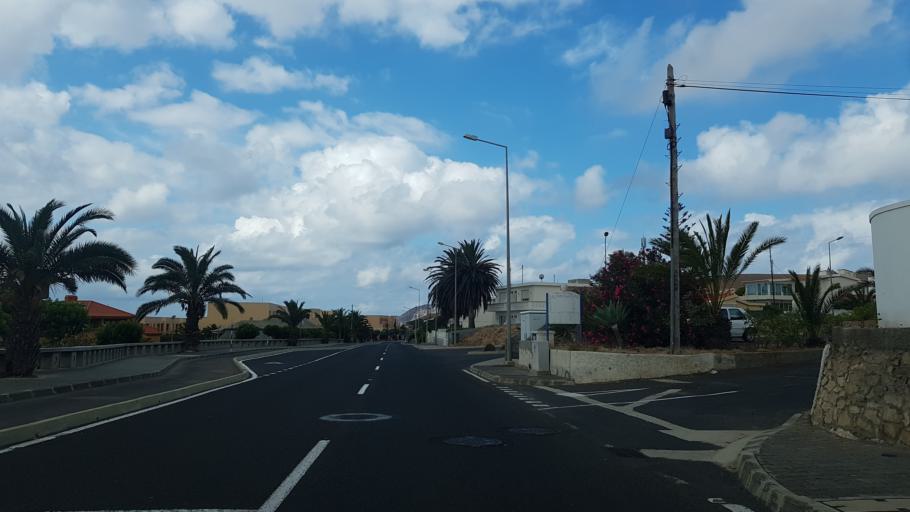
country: PT
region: Madeira
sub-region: Porto Santo
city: Vila de Porto Santo
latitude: 33.0452
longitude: -16.3567
